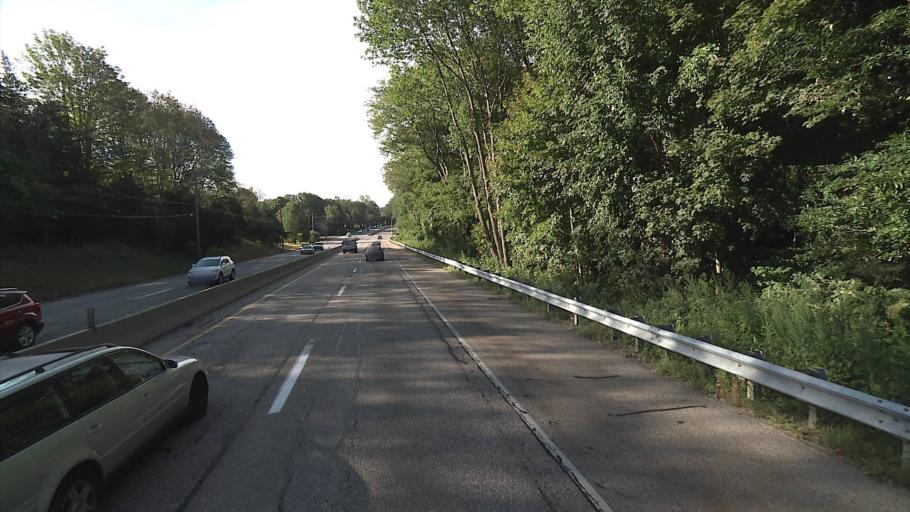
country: US
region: Connecticut
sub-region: New London County
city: Uncasville
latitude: 41.4053
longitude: -72.1062
